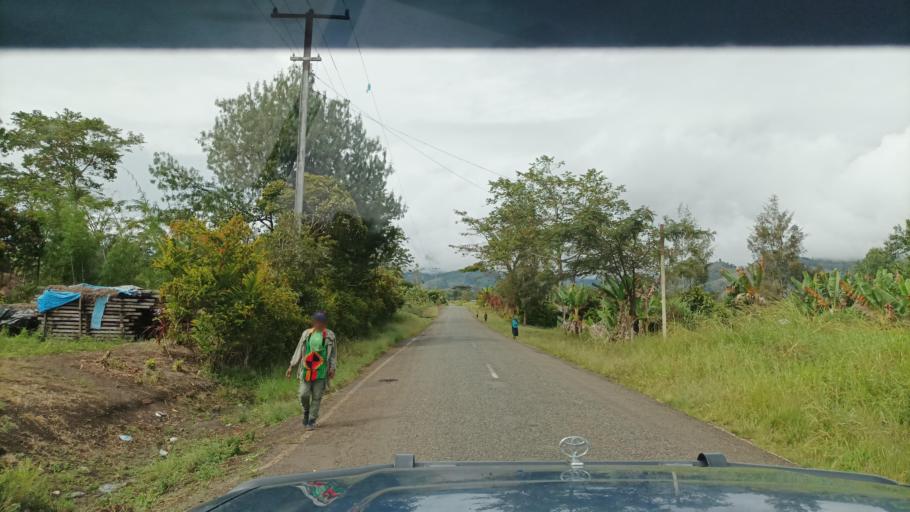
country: PG
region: Jiwaka
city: Minj
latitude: -5.8908
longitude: 144.6816
